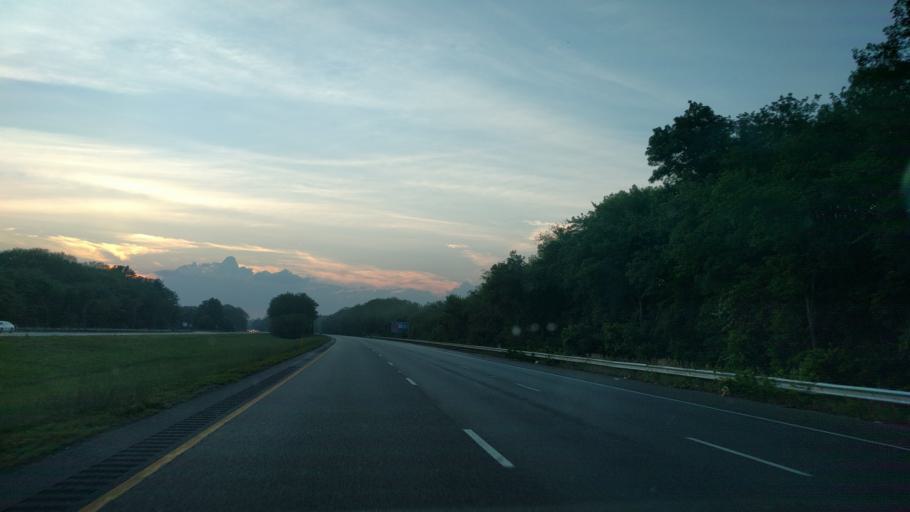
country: US
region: Massachusetts
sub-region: Bristol County
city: Ocean Grove
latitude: 41.7619
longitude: -71.2314
